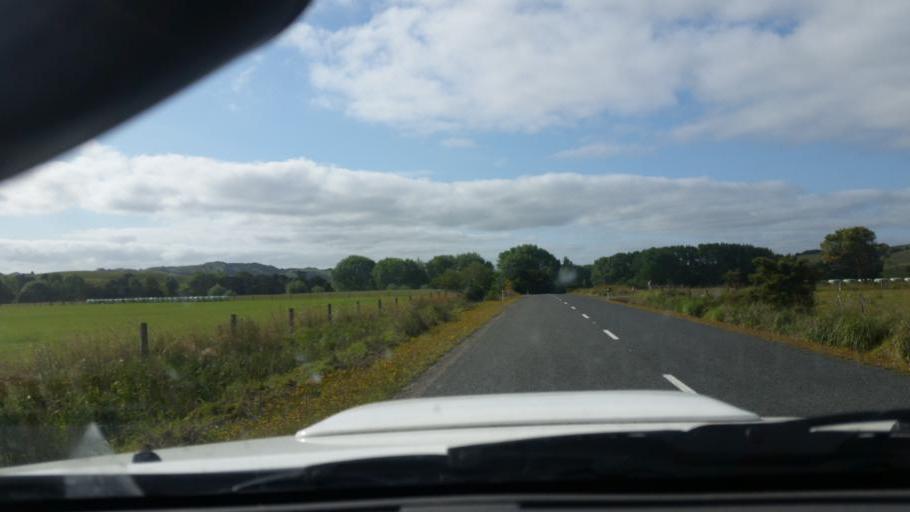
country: NZ
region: Northland
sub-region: Kaipara District
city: Dargaville
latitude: -35.8369
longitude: 173.8437
